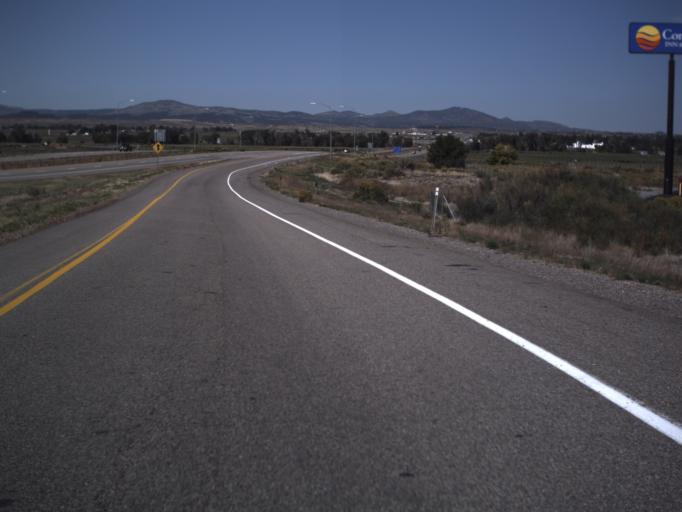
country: US
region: Utah
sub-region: Beaver County
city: Beaver
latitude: 38.2501
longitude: -112.6493
